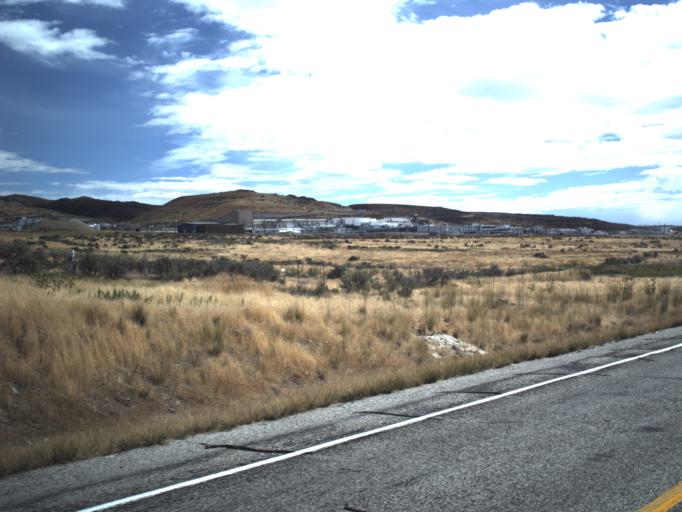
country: US
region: Utah
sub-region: Box Elder County
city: Tremonton
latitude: 41.6694
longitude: -112.4465
